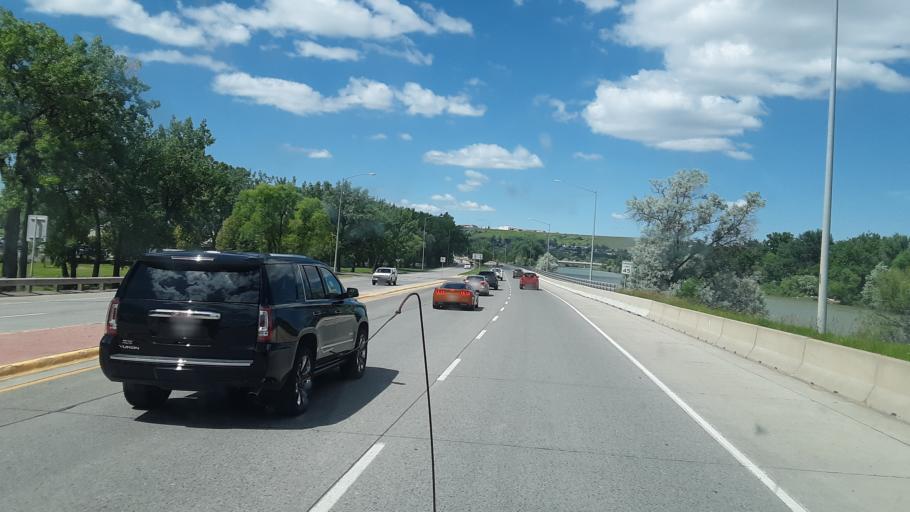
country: US
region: Montana
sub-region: Cascade County
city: Great Falls
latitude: 47.4930
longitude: -111.3167
